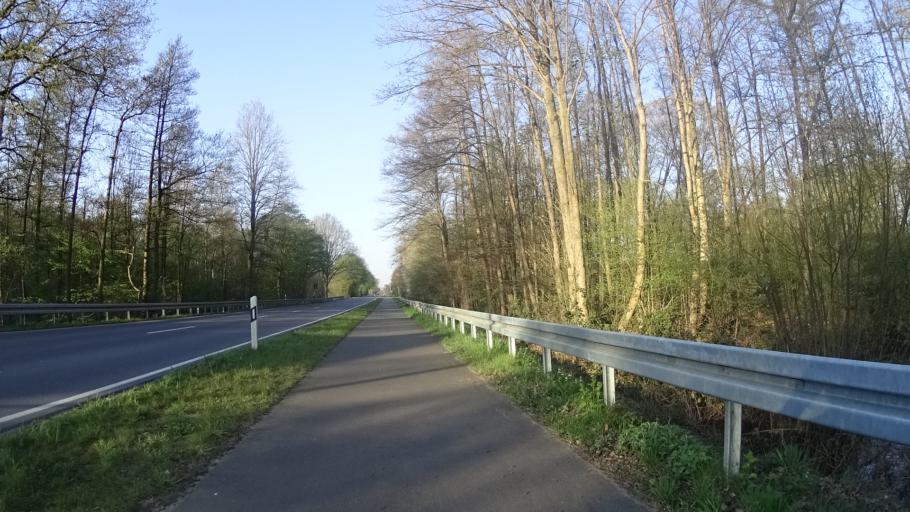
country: DE
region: North Rhine-Westphalia
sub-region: Regierungsbezirk Dusseldorf
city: Hunxe
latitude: 51.6601
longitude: 6.8075
